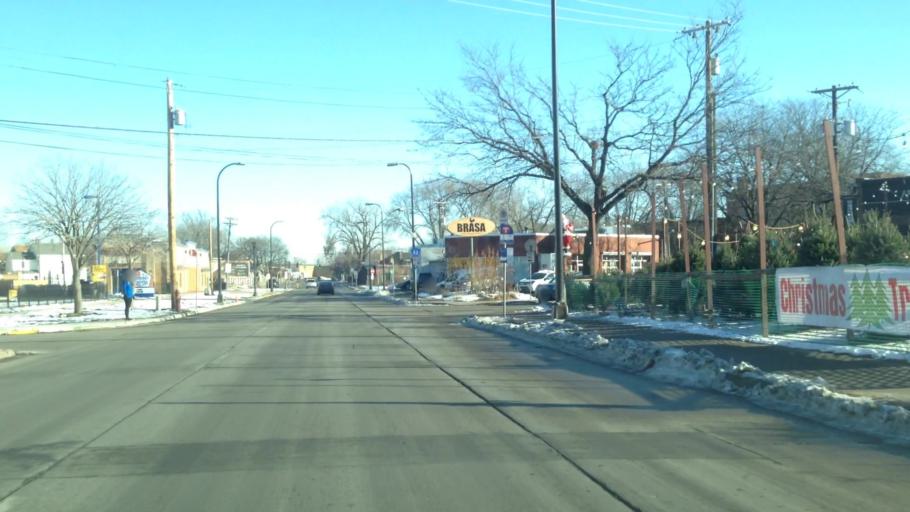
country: US
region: Minnesota
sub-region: Hennepin County
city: Minneapolis
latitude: 44.9893
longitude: -93.2523
